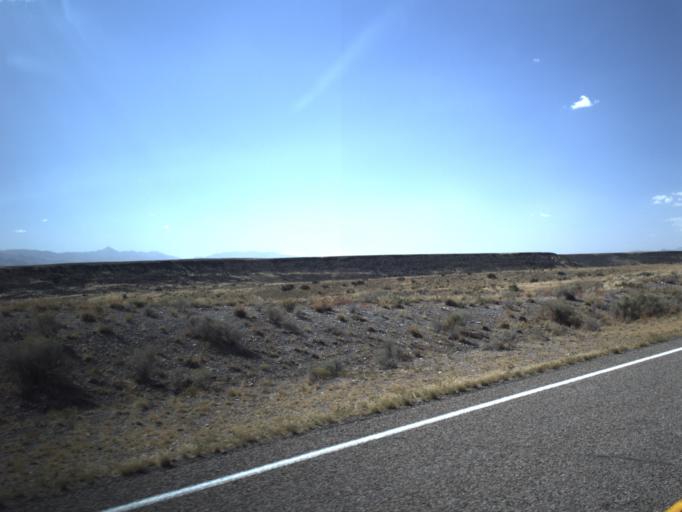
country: US
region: Utah
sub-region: Beaver County
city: Milford
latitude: 38.7730
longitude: -112.9318
